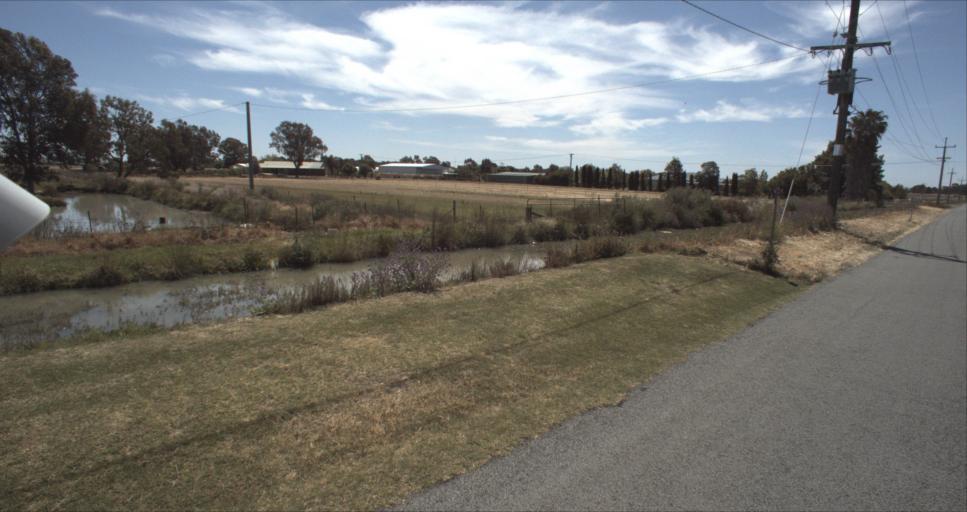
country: AU
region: New South Wales
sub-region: Leeton
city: Leeton
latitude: -34.5763
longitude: 146.4214
